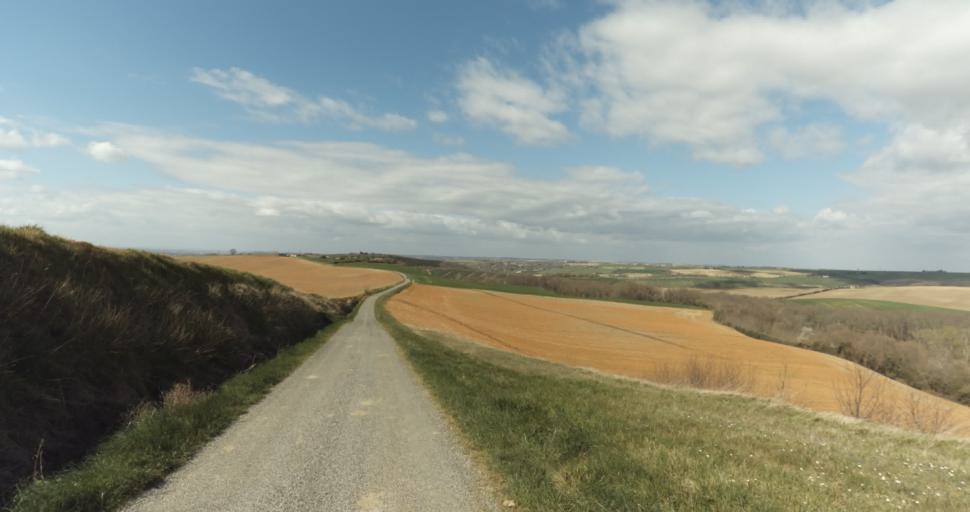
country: FR
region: Midi-Pyrenees
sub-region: Departement de la Haute-Garonne
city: Auterive
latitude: 43.3582
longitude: 1.5160
